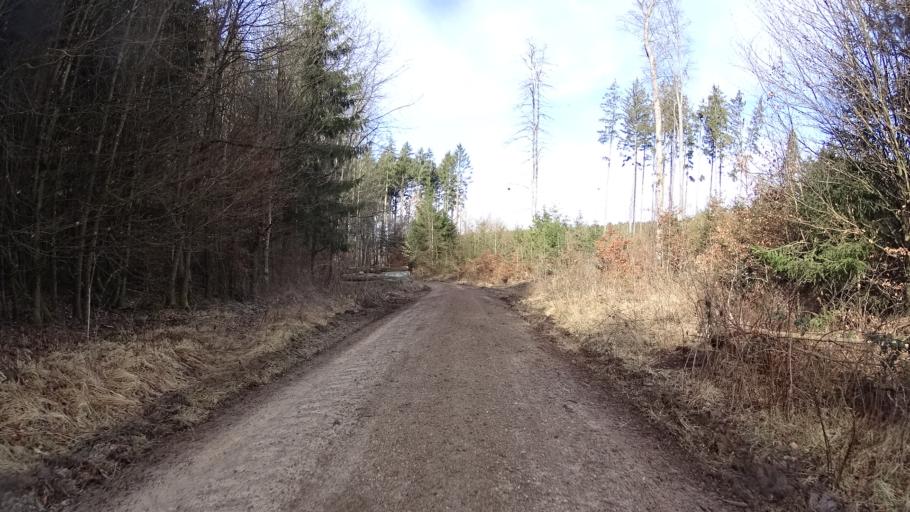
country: DE
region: Bavaria
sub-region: Upper Bavaria
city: Hitzhofen
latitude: 48.8833
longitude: 11.3108
